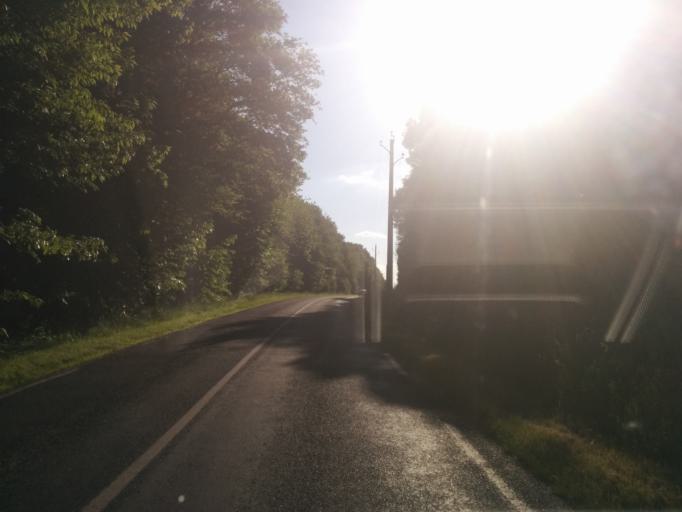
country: FR
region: Haute-Normandie
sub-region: Departement de l'Eure
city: Gasny
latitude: 49.0953
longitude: 1.5807
